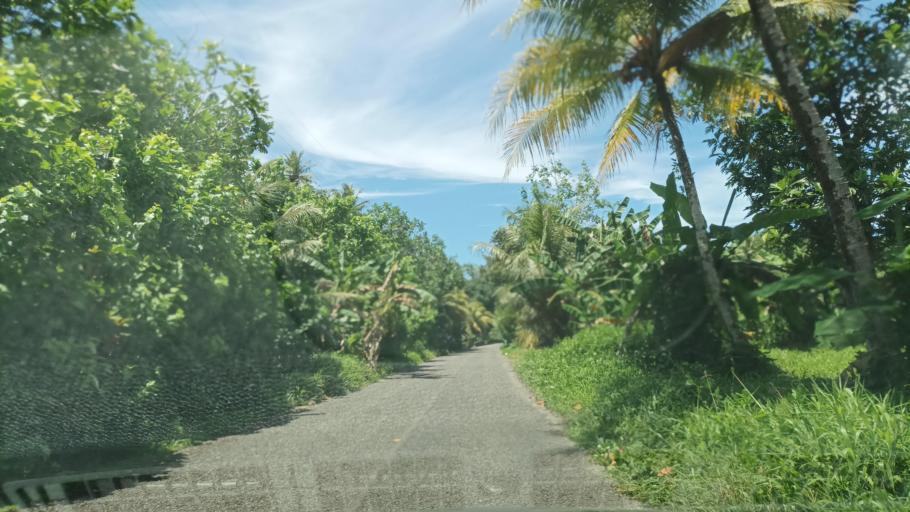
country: FM
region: Kosrae
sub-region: Malem Municipality
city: Malem
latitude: 5.3002
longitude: 163.0300
